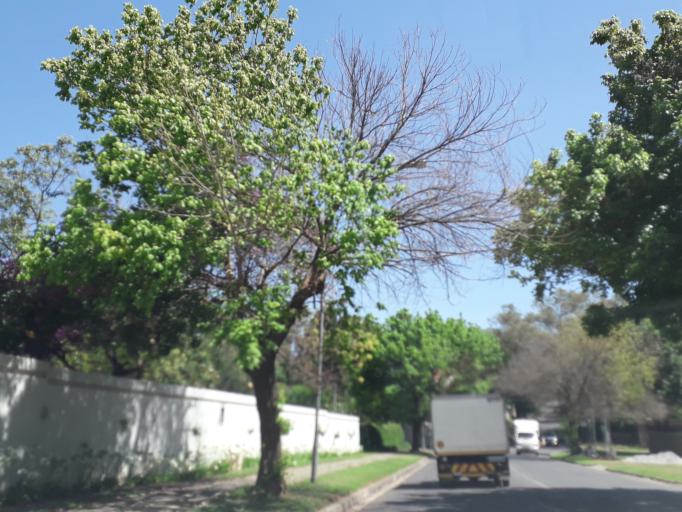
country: ZA
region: Gauteng
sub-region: City of Johannesburg Metropolitan Municipality
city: Johannesburg
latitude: -26.1331
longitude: 28.0296
